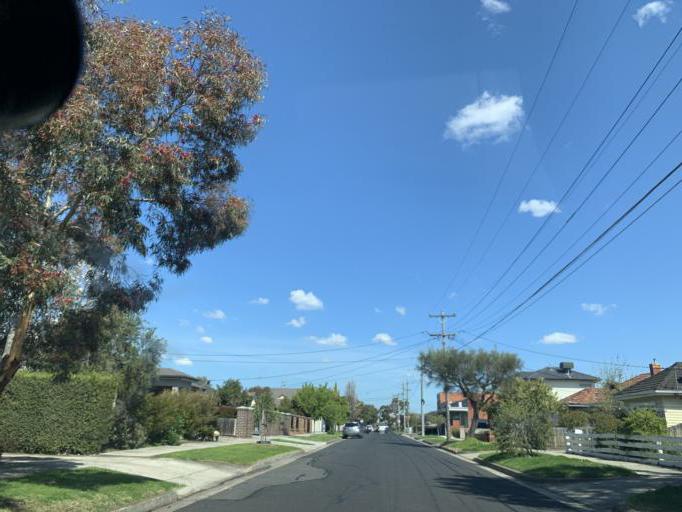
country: AU
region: Victoria
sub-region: Moreland
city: Pascoe Vale
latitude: -37.7357
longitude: 144.9350
